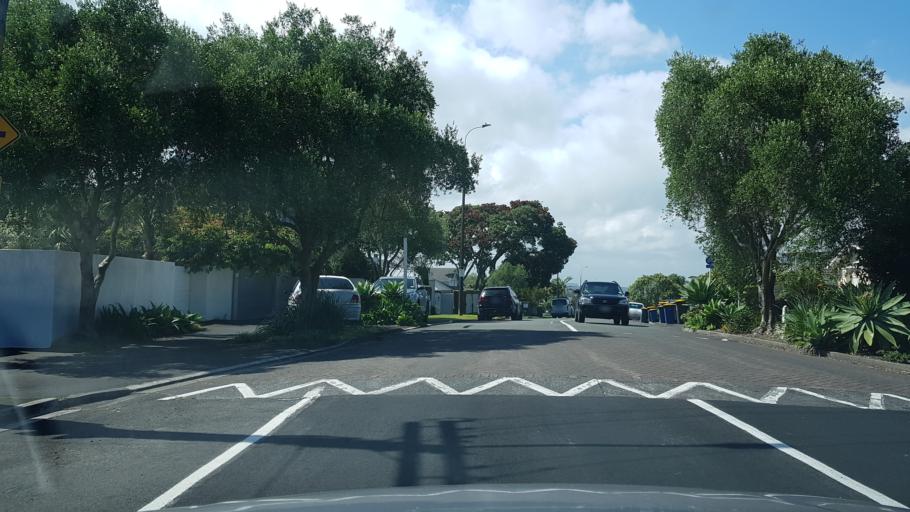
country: NZ
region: Auckland
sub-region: Auckland
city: North Shore
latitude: -36.8092
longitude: 174.7978
